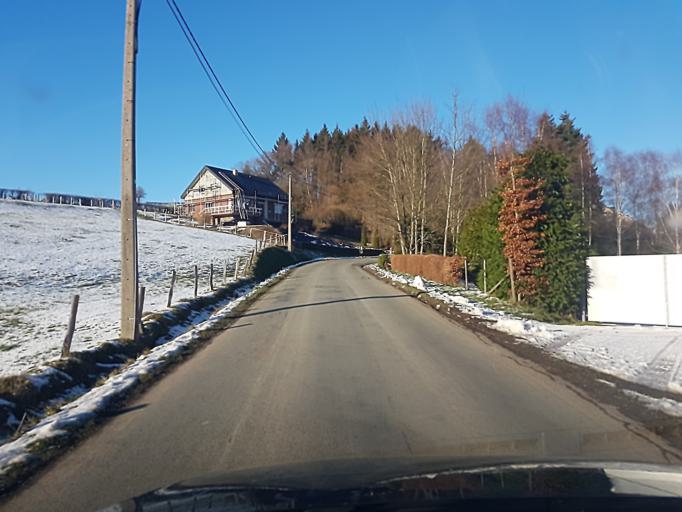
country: BE
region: Wallonia
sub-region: Province de Liege
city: Jalhay
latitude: 50.5446
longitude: 5.9654
